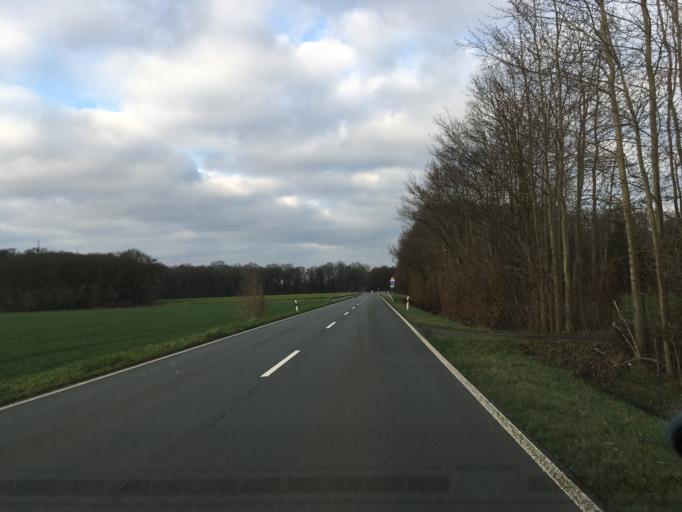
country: DE
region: North Rhine-Westphalia
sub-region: Regierungsbezirk Munster
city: Ahaus
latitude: 52.1430
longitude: 6.9888
